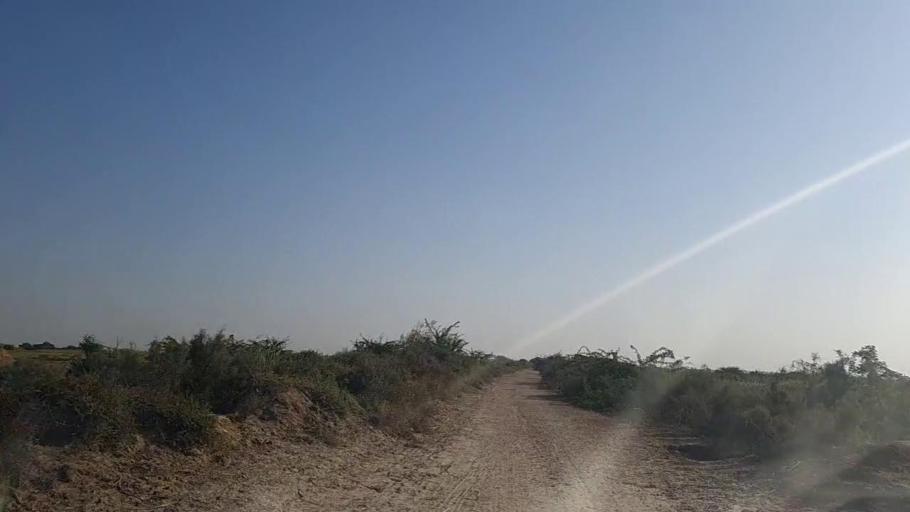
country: PK
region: Sindh
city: Jati
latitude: 24.3952
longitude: 68.2302
